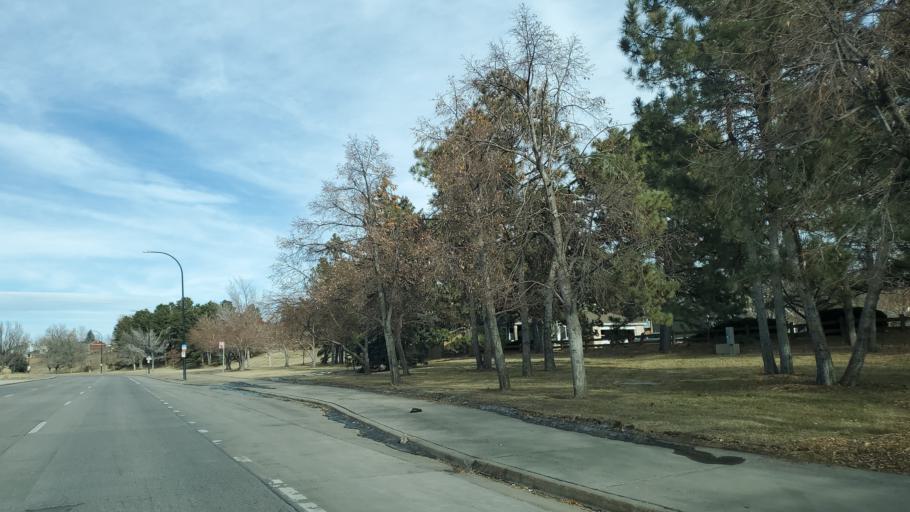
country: US
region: Colorado
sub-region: Douglas County
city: Highlands Ranch
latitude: 39.5586
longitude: -104.9876
